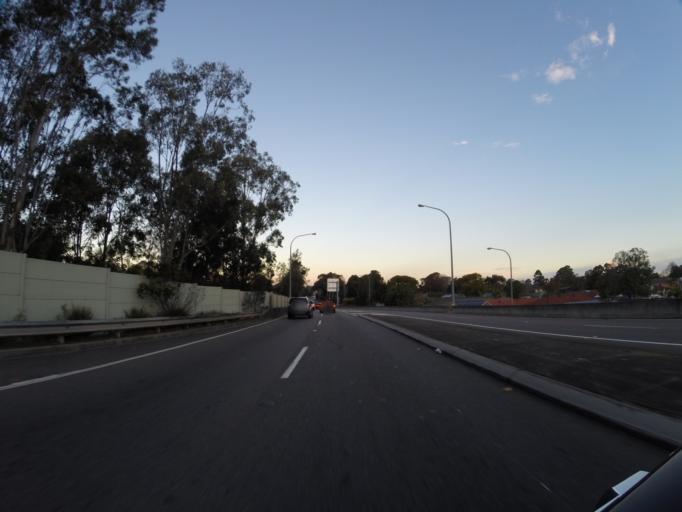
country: AU
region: New South Wales
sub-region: Bankstown
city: Milperra
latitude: -33.9429
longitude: 150.9434
